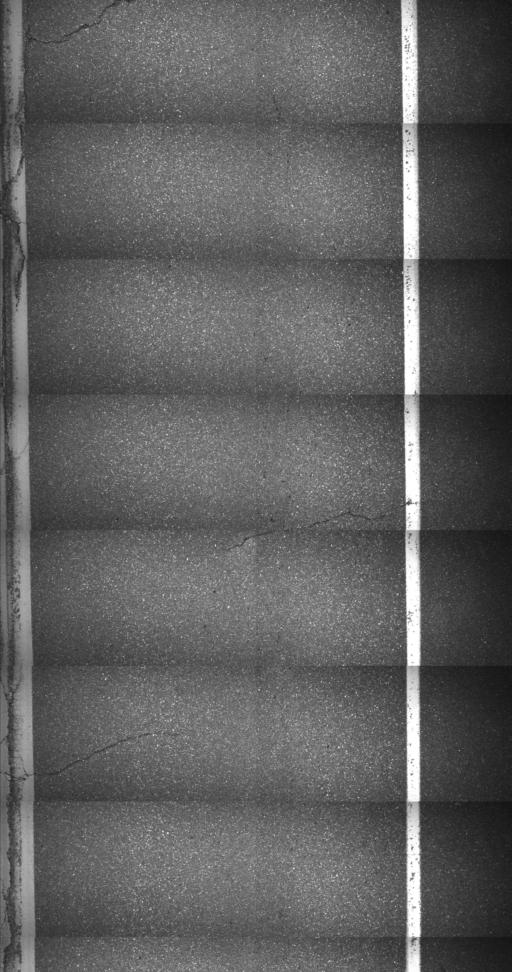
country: US
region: New Hampshire
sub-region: Coos County
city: Stratford
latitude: 44.7075
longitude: -71.6059
